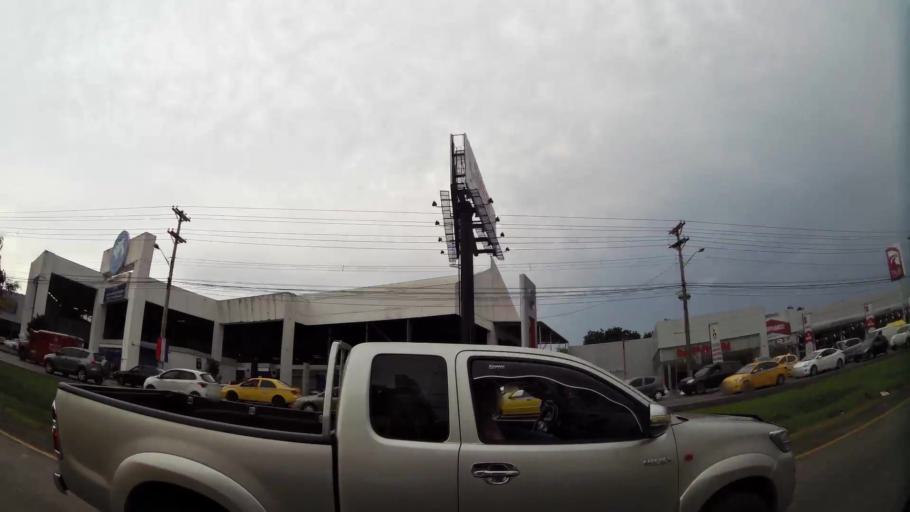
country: PA
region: Panama
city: Panama
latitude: 9.0181
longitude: -79.5347
